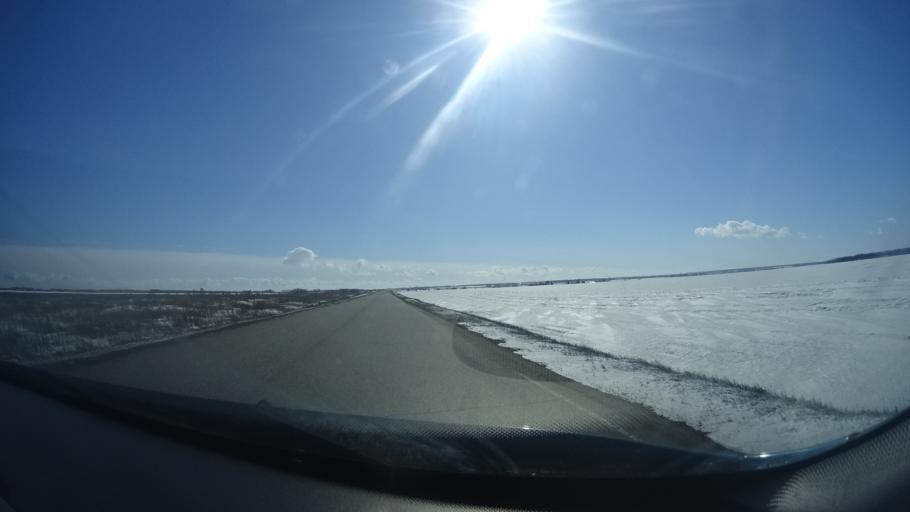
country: RU
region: Bashkortostan
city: Avdon
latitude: 54.5954
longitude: 55.8527
